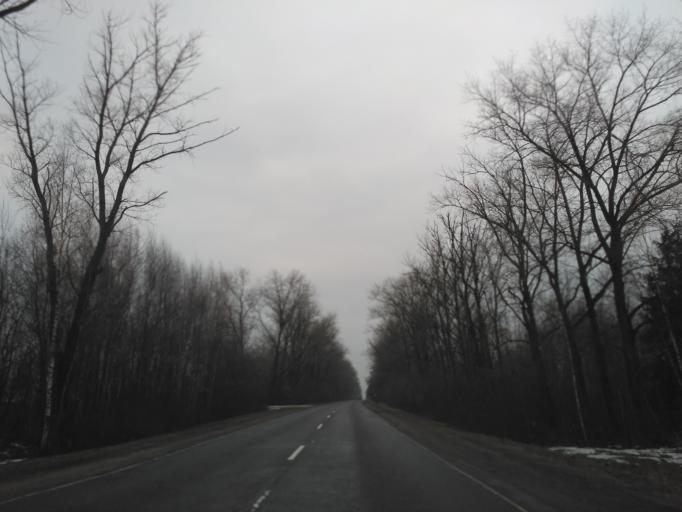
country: BY
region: Minsk
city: Snow
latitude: 53.2653
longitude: 26.3266
